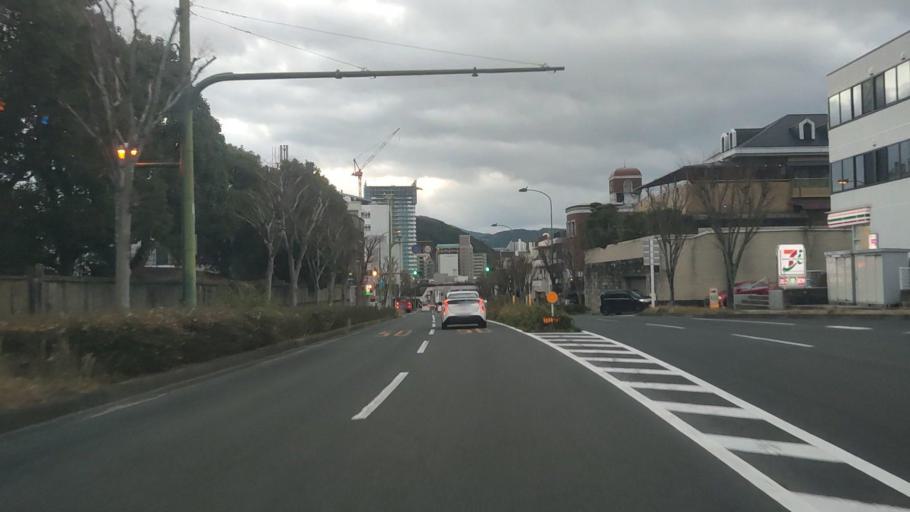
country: JP
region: Nagasaki
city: Nagasaki-shi
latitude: 32.7587
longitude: 129.8867
